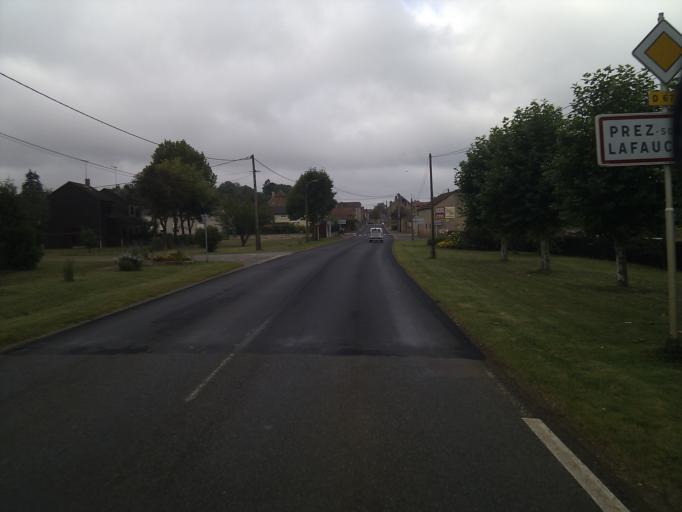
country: FR
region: Lorraine
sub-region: Departement des Vosges
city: Liffol-le-Grand
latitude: 48.2873
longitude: 5.4976
